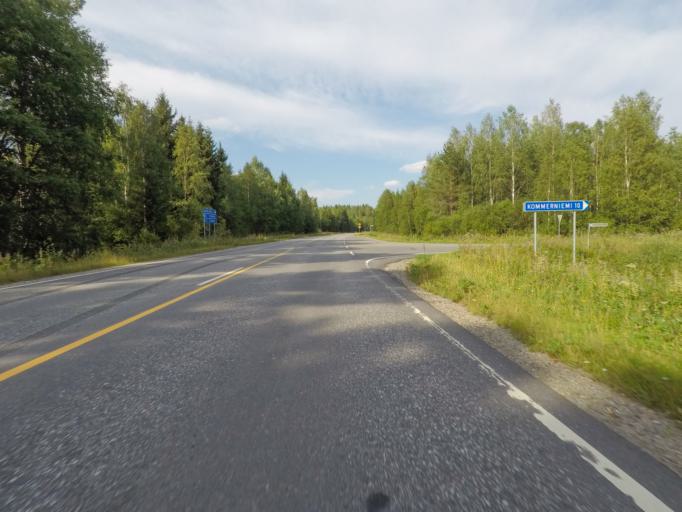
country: FI
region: Southern Savonia
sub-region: Savonlinna
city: Sulkava
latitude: 61.8661
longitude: 28.4733
